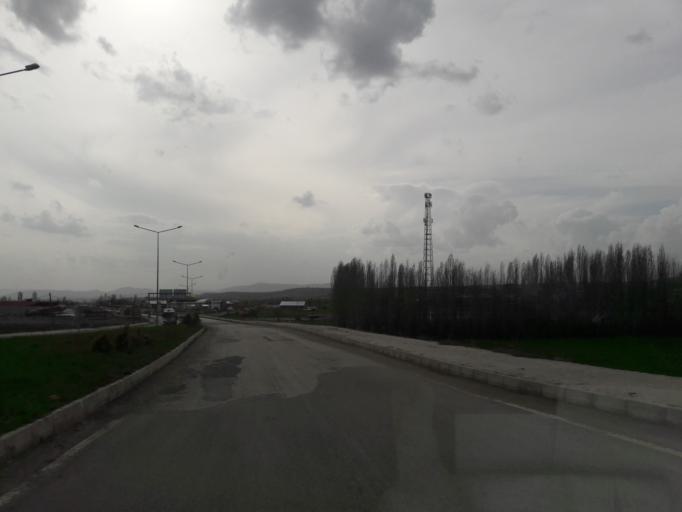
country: TR
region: Gumushane
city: Siran
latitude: 40.1793
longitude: 39.1222
